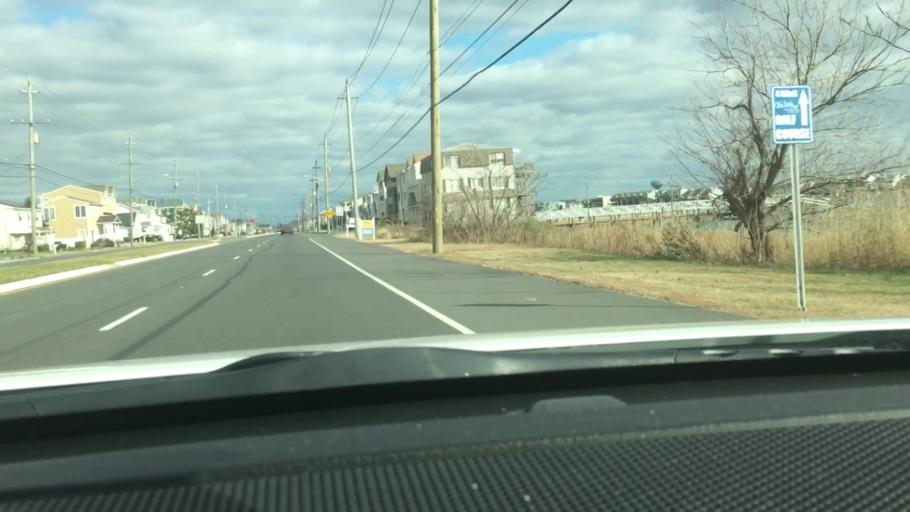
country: US
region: New Jersey
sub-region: Atlantic County
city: Atlantic City
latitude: 39.3901
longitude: -74.4124
